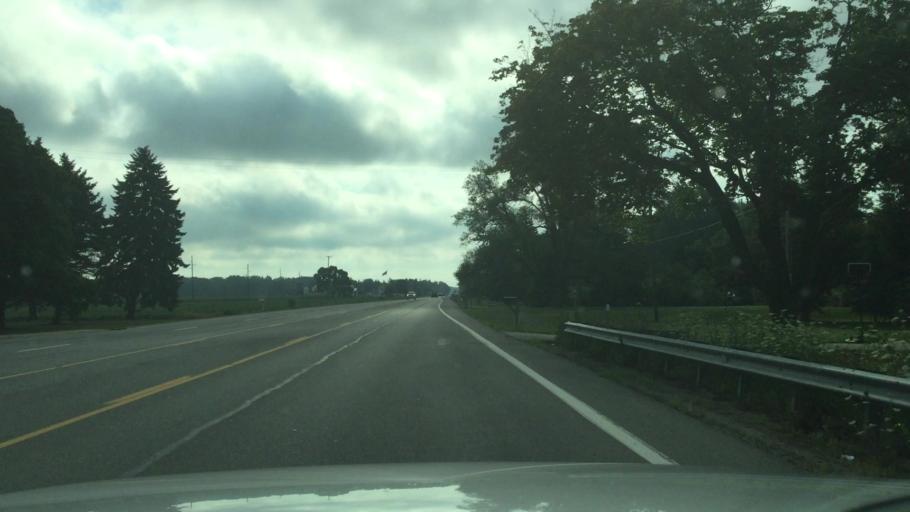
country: US
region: Michigan
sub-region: Saginaw County
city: Birch Run
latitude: 43.2502
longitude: -83.7651
